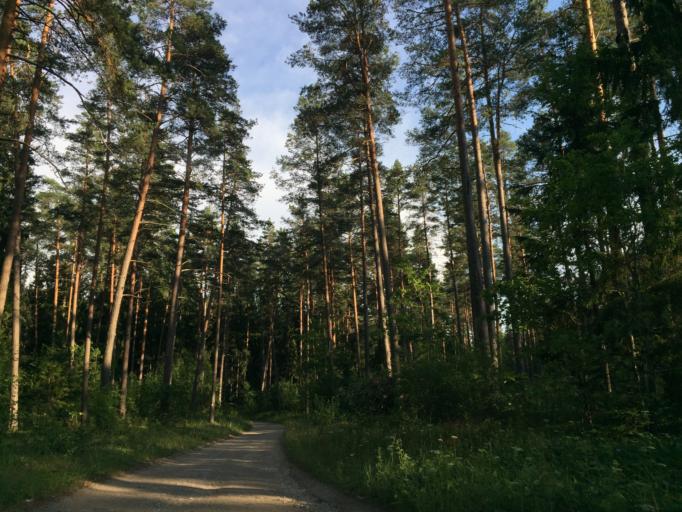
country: LV
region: Krimulda
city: Ragana
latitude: 57.1408
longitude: 24.7655
